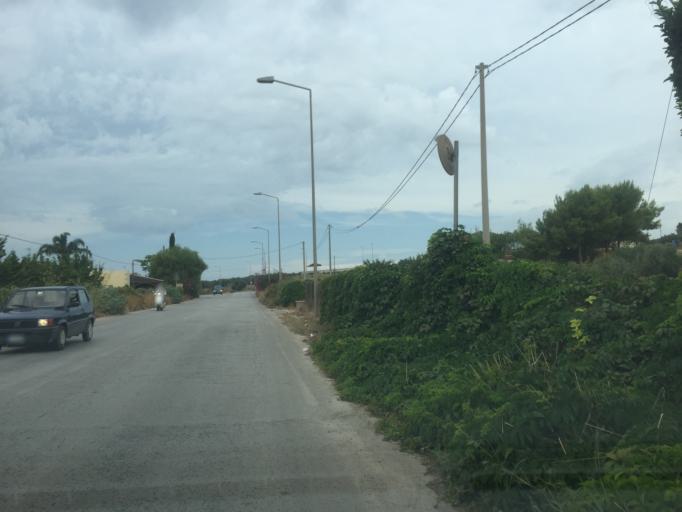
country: IT
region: Sicily
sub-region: Ragusa
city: Donnalucata
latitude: 36.7762
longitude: 14.6067
